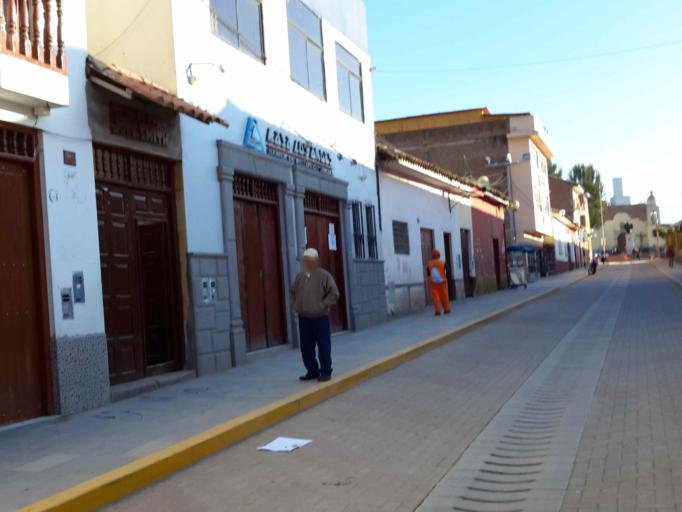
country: PE
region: Ayacucho
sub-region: Provincia de Huamanga
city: Ayacucho
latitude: -13.1558
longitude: -74.2253
